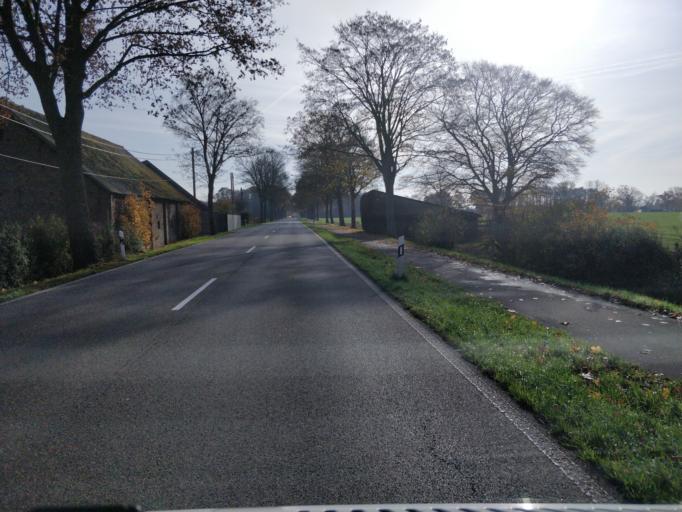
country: DE
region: North Rhine-Westphalia
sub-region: Regierungsbezirk Dusseldorf
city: Mehrhoog
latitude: 51.7271
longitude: 6.5073
